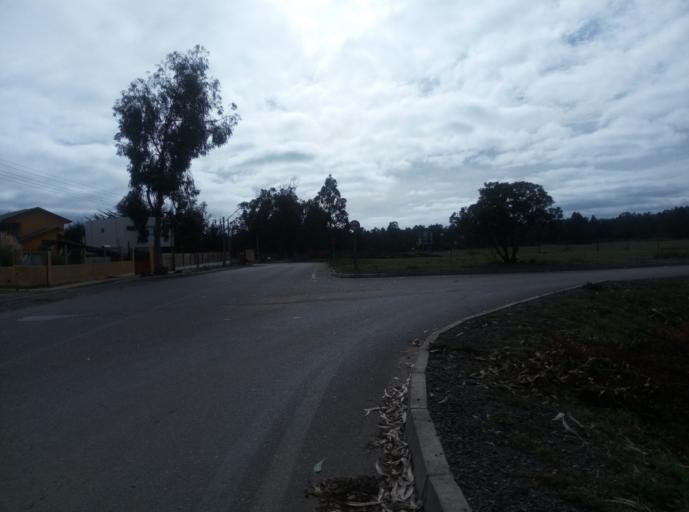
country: CL
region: Valparaiso
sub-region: San Antonio Province
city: El Tabo
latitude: -33.4248
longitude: -71.6876
